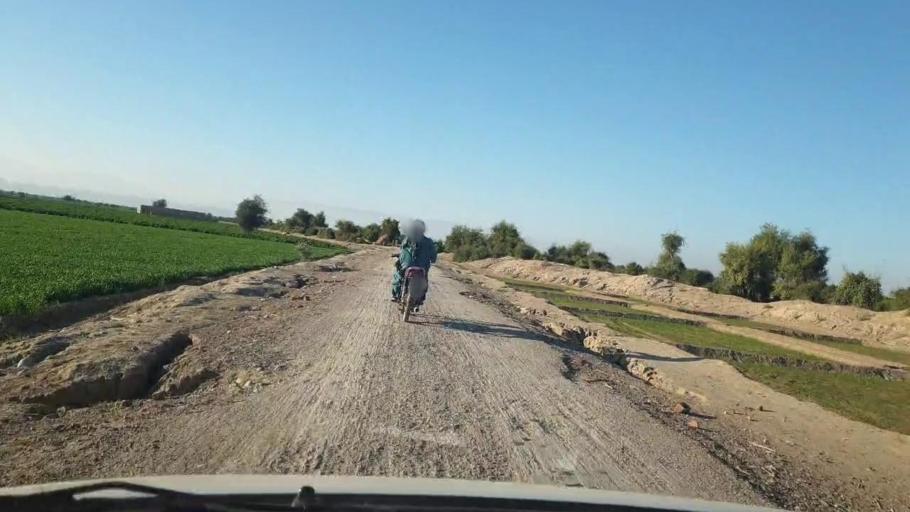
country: PK
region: Sindh
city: Johi
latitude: 26.7650
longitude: 67.4642
